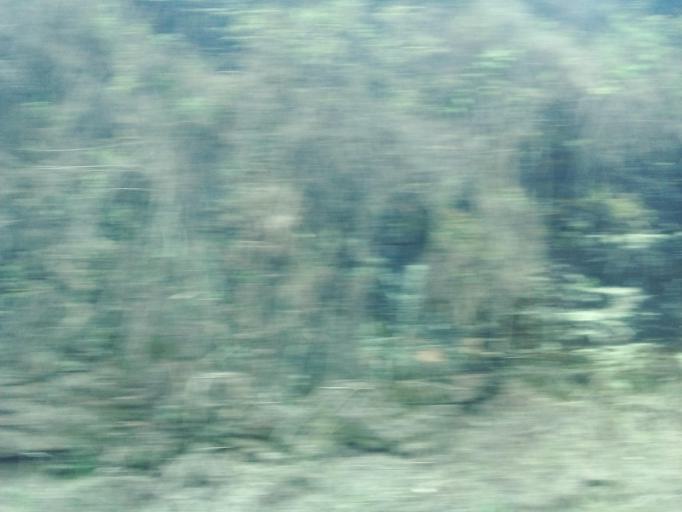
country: BR
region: Minas Gerais
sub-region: Rio Piracicaba
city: Rio Piracicaba
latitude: -19.8975
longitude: -43.1435
